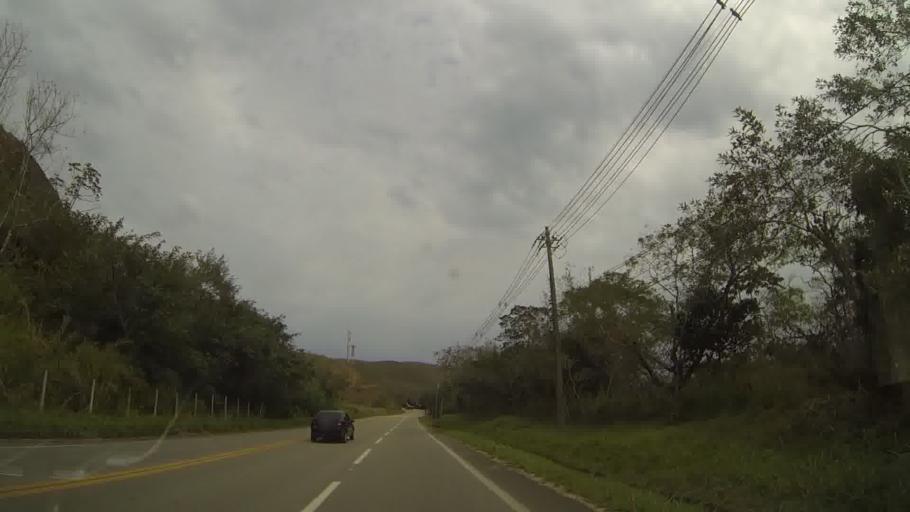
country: BR
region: Sao Paulo
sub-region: Sao Sebastiao
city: Sao Sebastiao
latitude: -23.8012
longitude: -45.5448
